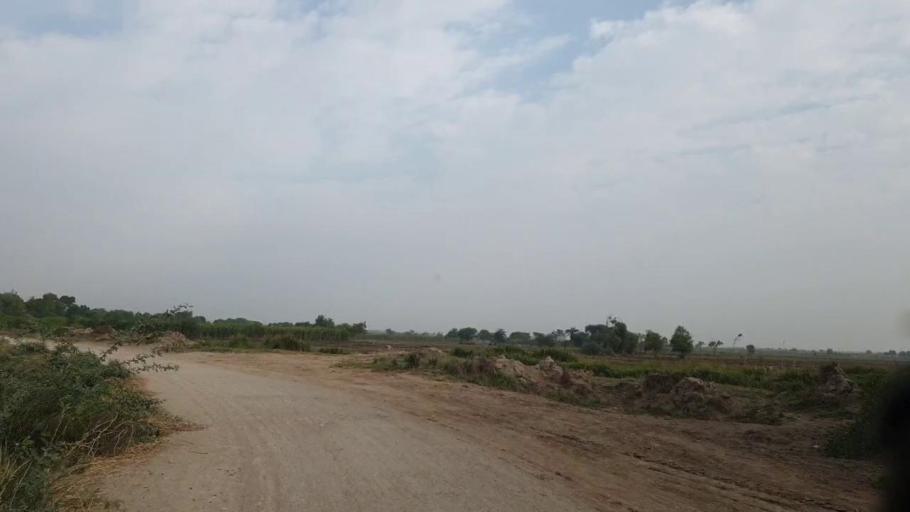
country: PK
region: Sindh
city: Tando Muhammad Khan
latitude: 25.0940
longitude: 68.4180
